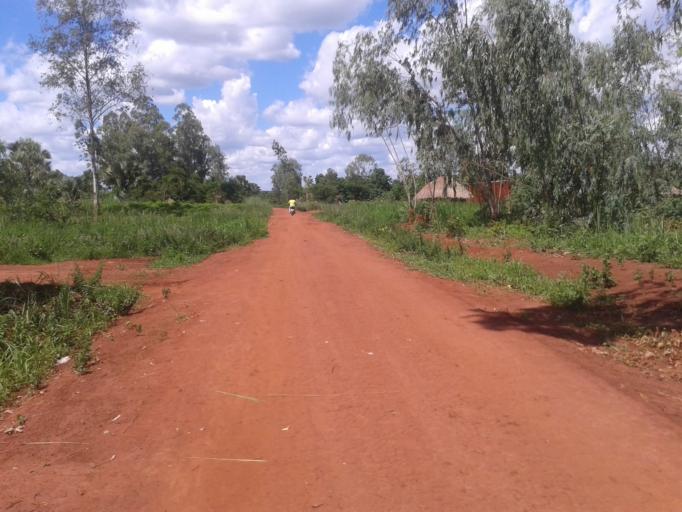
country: UG
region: Northern Region
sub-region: Gulu District
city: Gulu
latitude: 2.7581
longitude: 32.3269
